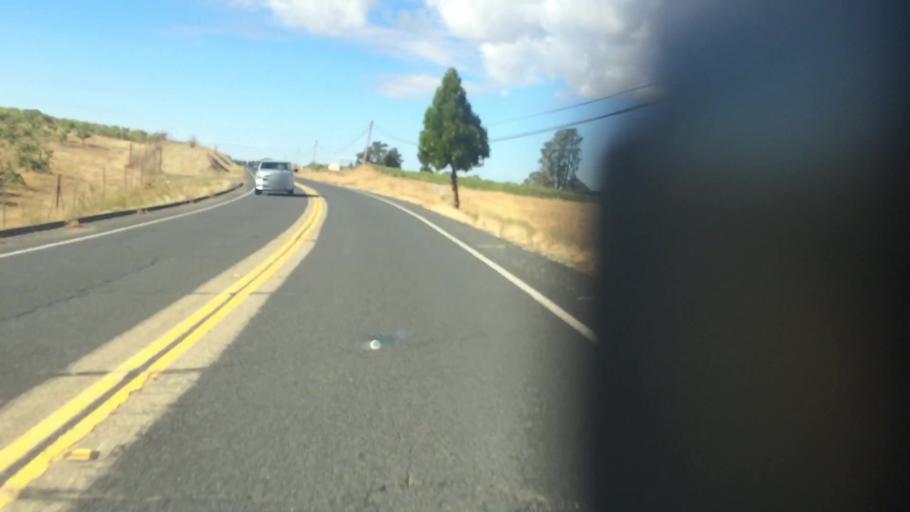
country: US
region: California
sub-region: Amador County
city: Plymouth
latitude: 38.5305
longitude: -120.8066
